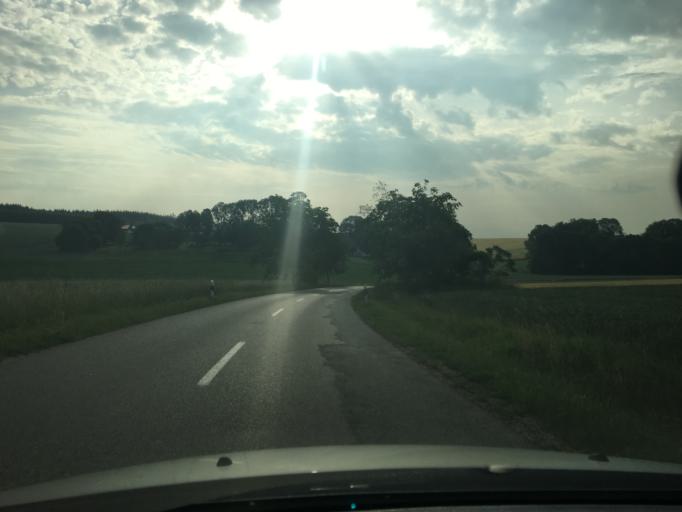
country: DE
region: Bavaria
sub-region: Lower Bavaria
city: Bodenkirchen
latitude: 48.3788
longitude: 12.4073
